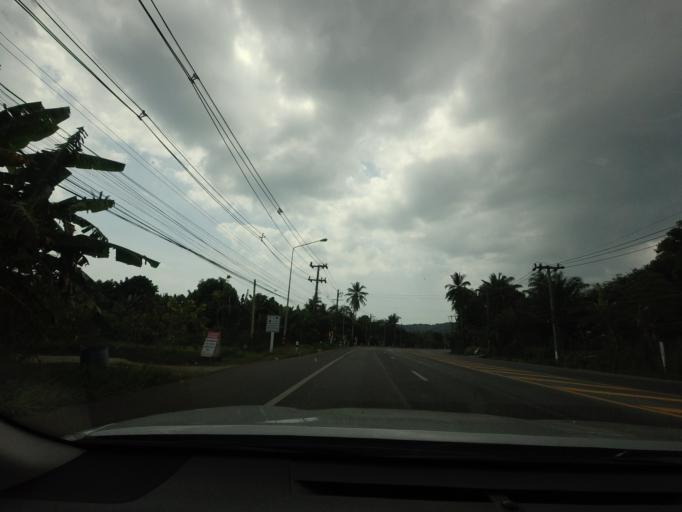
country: TH
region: Phangnga
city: Ban Ao Nang
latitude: 8.0582
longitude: 98.7819
